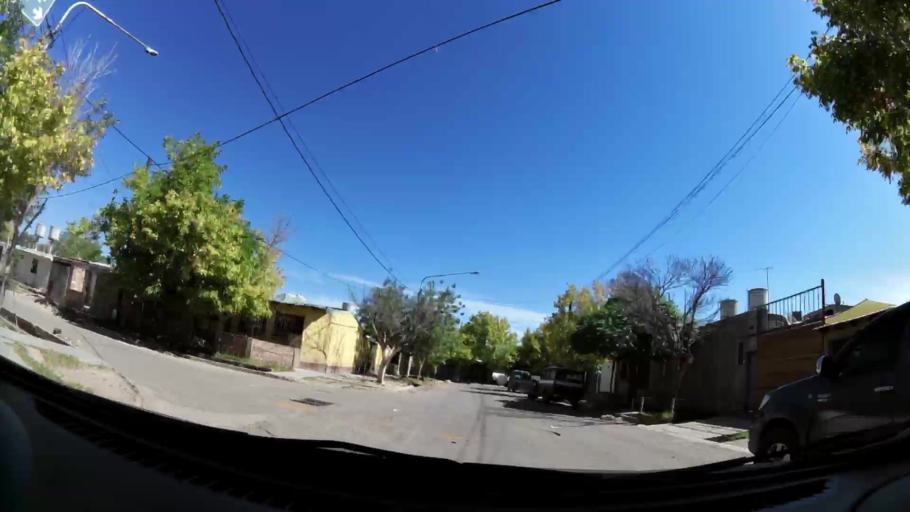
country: AR
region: Mendoza
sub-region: Departamento de Godoy Cruz
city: Godoy Cruz
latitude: -32.9668
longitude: -68.8340
